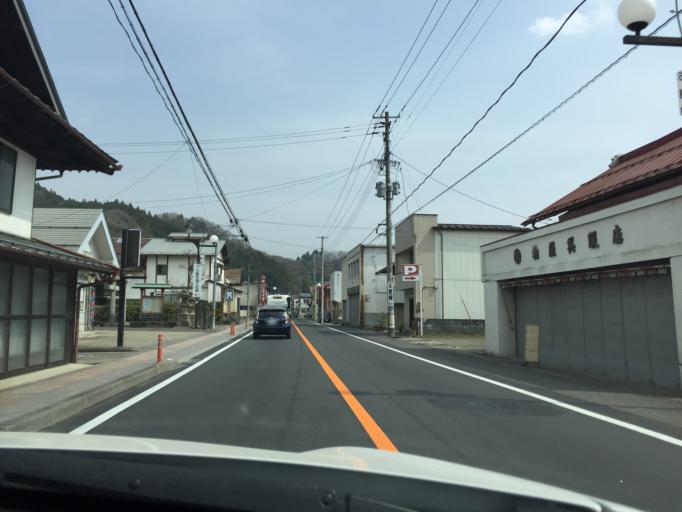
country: JP
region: Fukushima
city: Ishikawa
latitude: 37.0928
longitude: 140.5496
